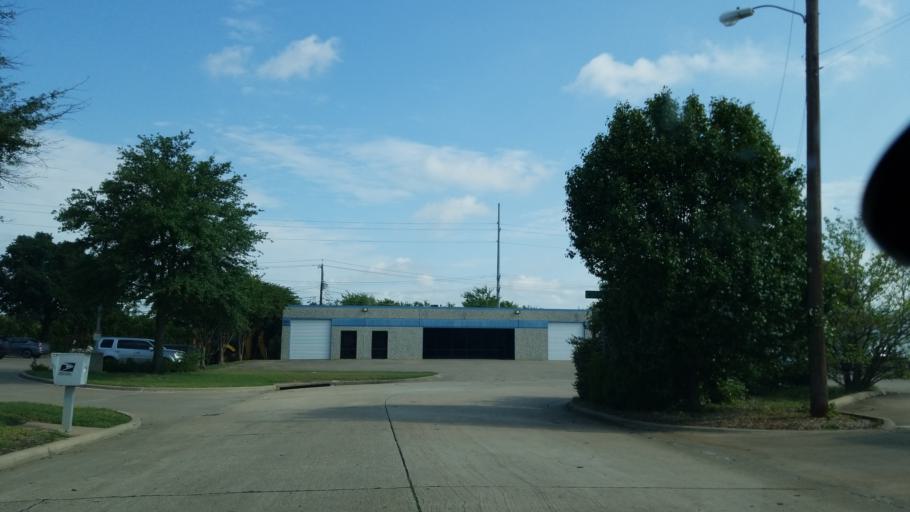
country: US
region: Texas
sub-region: Dallas County
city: Garland
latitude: 32.9119
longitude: -96.6596
